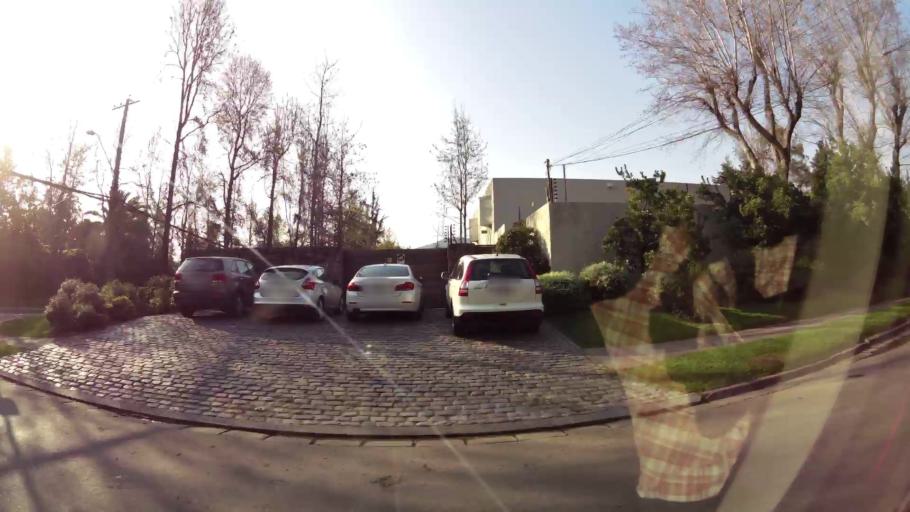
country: CL
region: Santiago Metropolitan
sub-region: Provincia de Santiago
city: Villa Presidente Frei, Nunoa, Santiago, Chile
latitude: -33.3592
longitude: -70.5302
